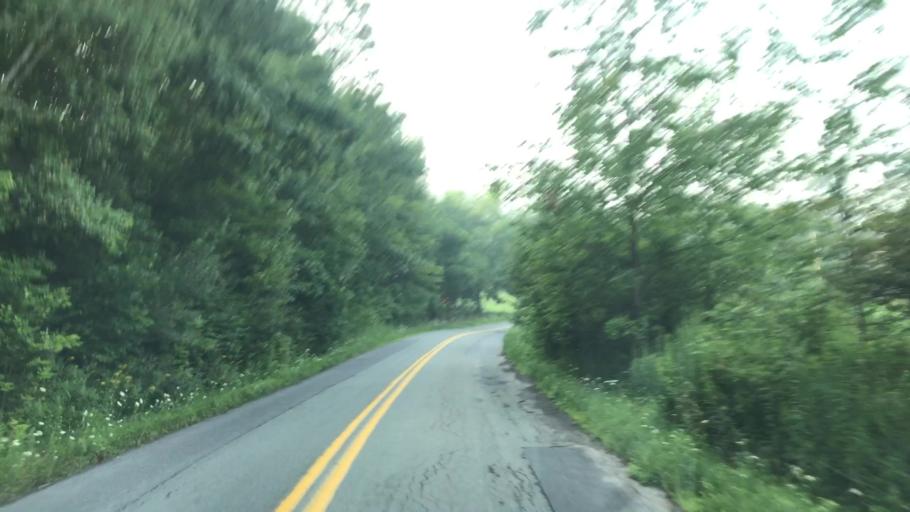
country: US
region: Pennsylvania
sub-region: Wyoming County
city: Factoryville
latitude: 41.6485
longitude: -75.7948
